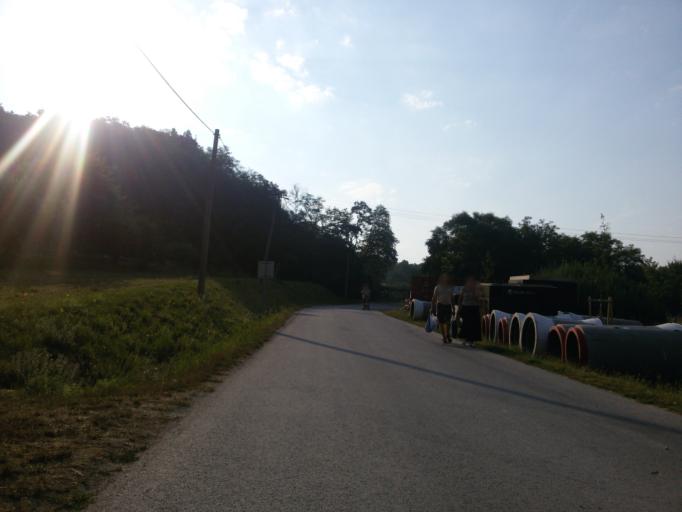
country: CZ
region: South Moravian
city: Kurim
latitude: 49.2992
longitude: 16.5466
